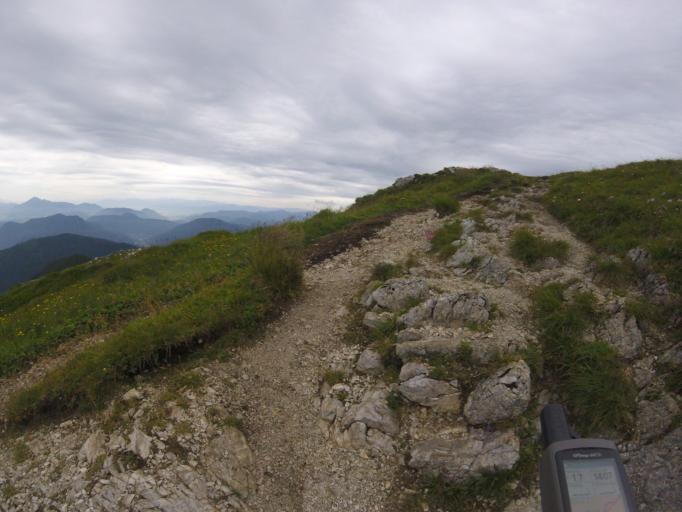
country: SK
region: Zilinsky
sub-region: Okres Zilina
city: Terchova
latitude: 49.1879
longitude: 19.0520
